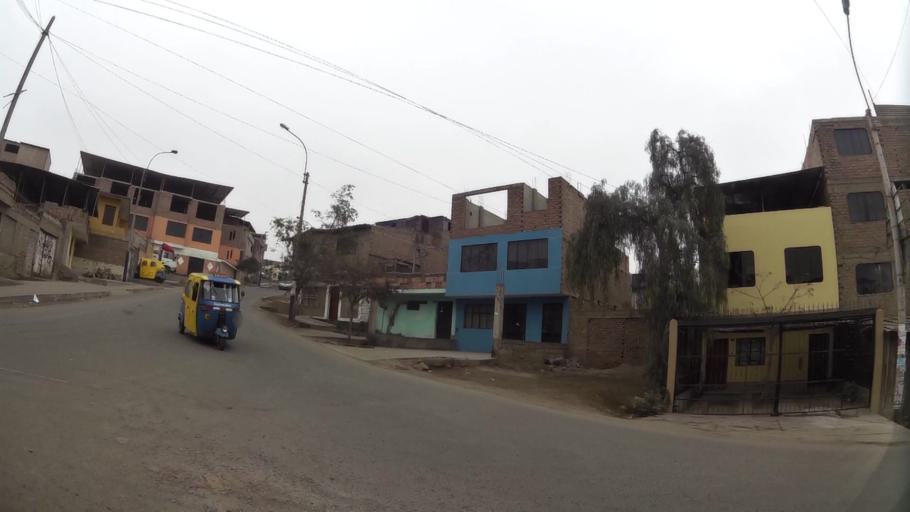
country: PE
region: Lima
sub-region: Lima
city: Surco
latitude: -12.1638
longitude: -76.9585
